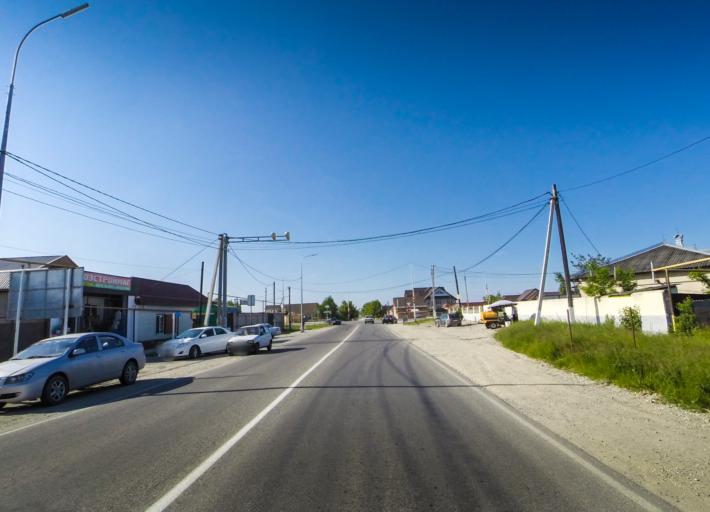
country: RU
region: Kabardino-Balkariya
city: Urvan'
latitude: 43.4954
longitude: 43.7640
